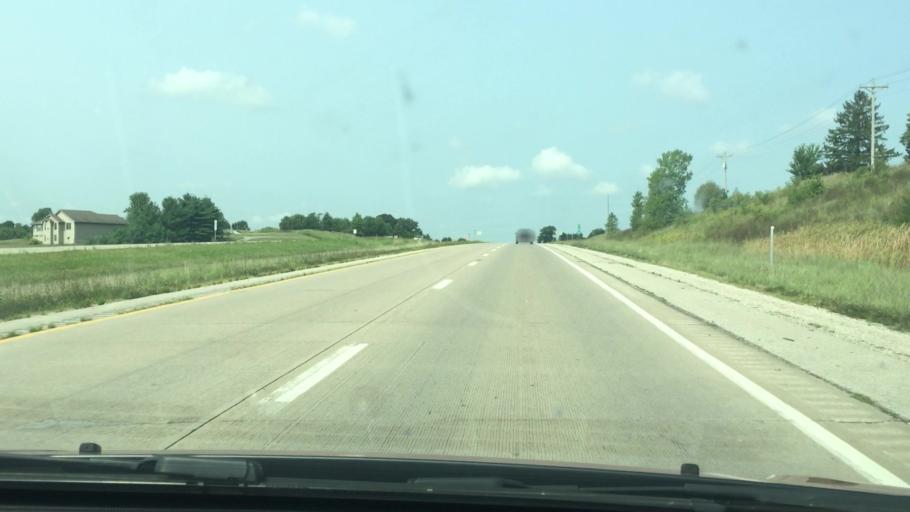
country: US
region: Iowa
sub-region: Scott County
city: Blue Grass
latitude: 41.5134
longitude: -90.8061
